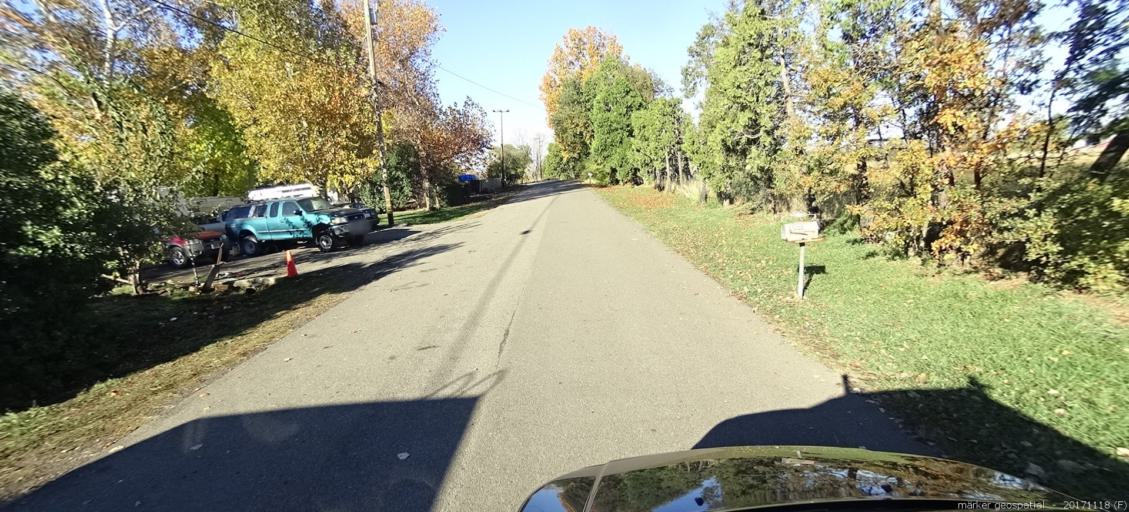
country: US
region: California
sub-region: Shasta County
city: Anderson
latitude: 40.4417
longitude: -122.2800
